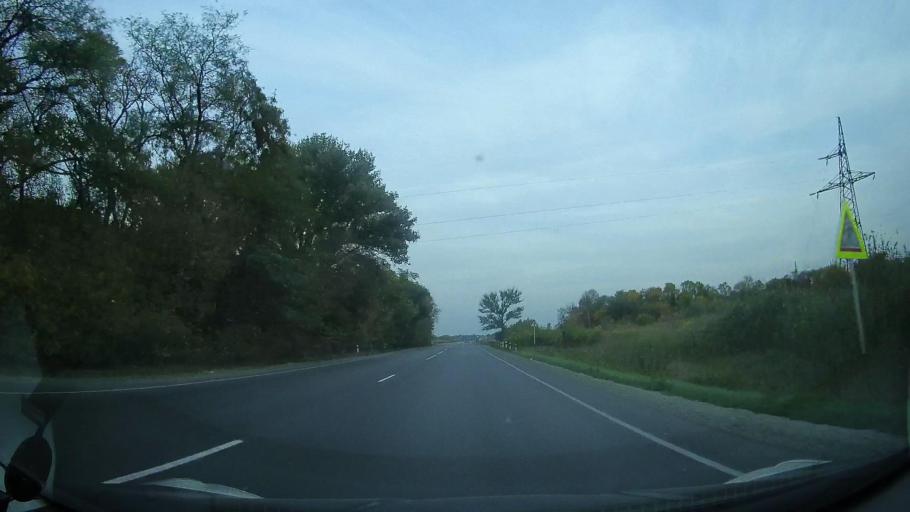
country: RU
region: Rostov
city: Ol'ginskaya
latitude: 47.1314
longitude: 39.9530
